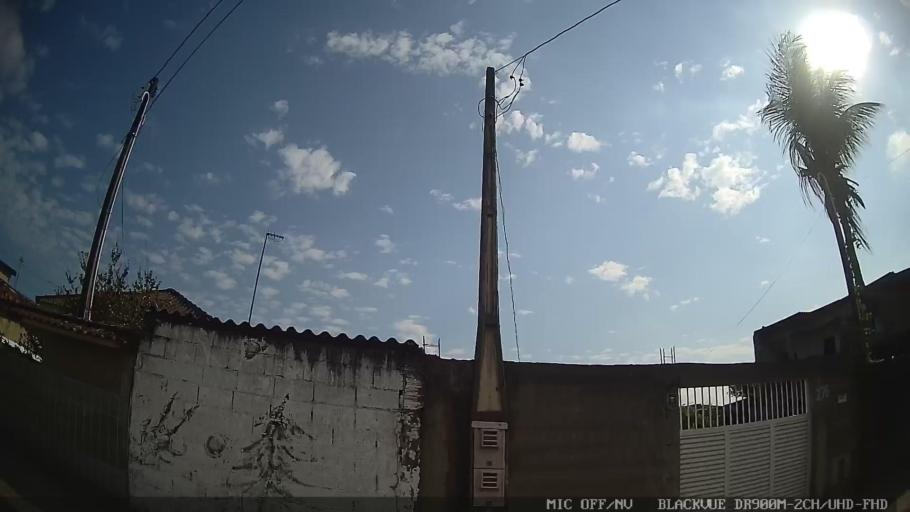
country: BR
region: Sao Paulo
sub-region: Santos
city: Santos
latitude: -23.9538
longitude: -46.2940
